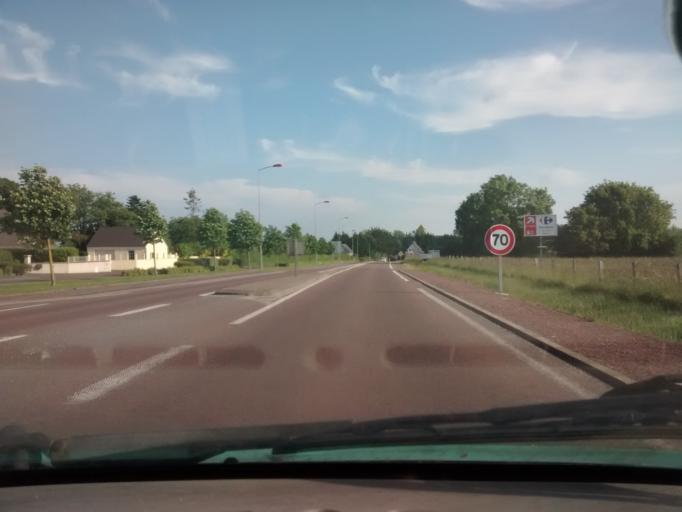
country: FR
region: Lower Normandy
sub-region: Departement de la Manche
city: Lessay
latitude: 49.2272
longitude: -1.5342
